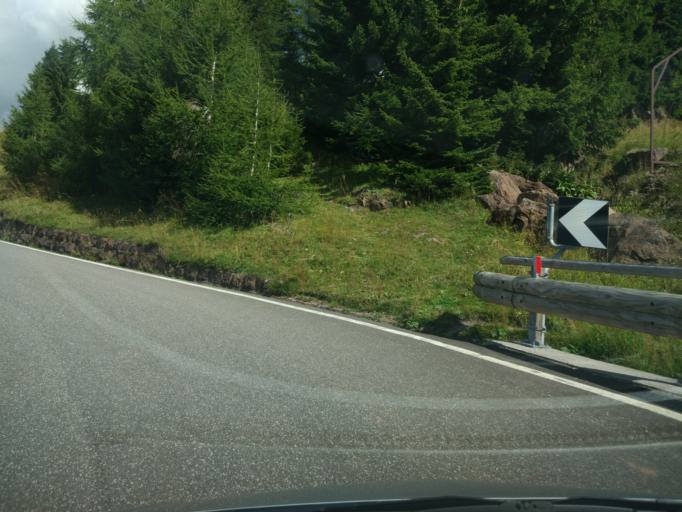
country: IT
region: Veneto
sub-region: Provincia di Belluno
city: Falcade Alto
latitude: 46.2954
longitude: 11.7800
